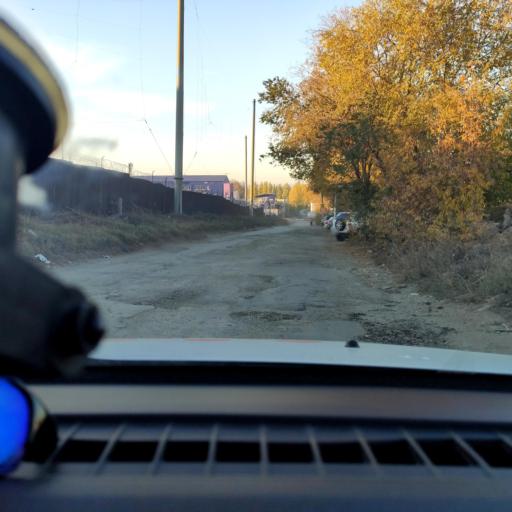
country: RU
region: Samara
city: Samara
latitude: 53.1828
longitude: 50.1527
